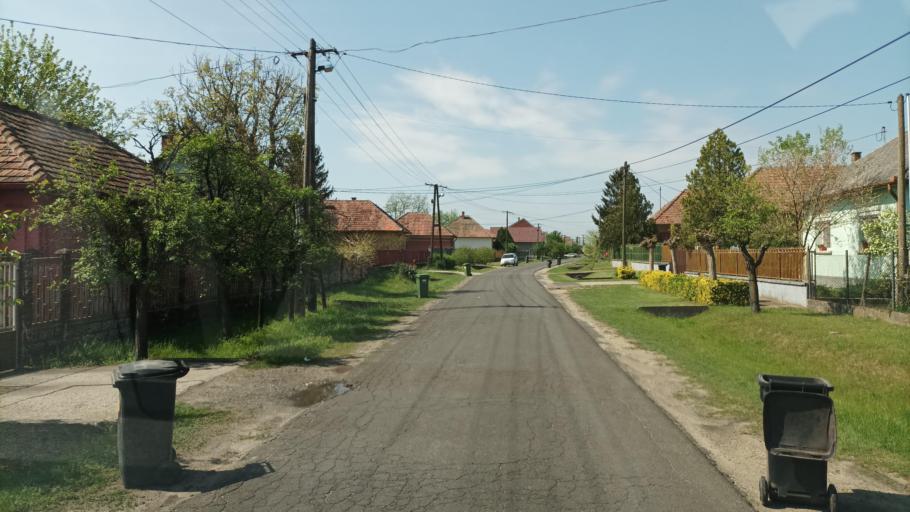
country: HU
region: Pest
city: Tapiosag
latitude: 47.4076
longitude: 19.6300
